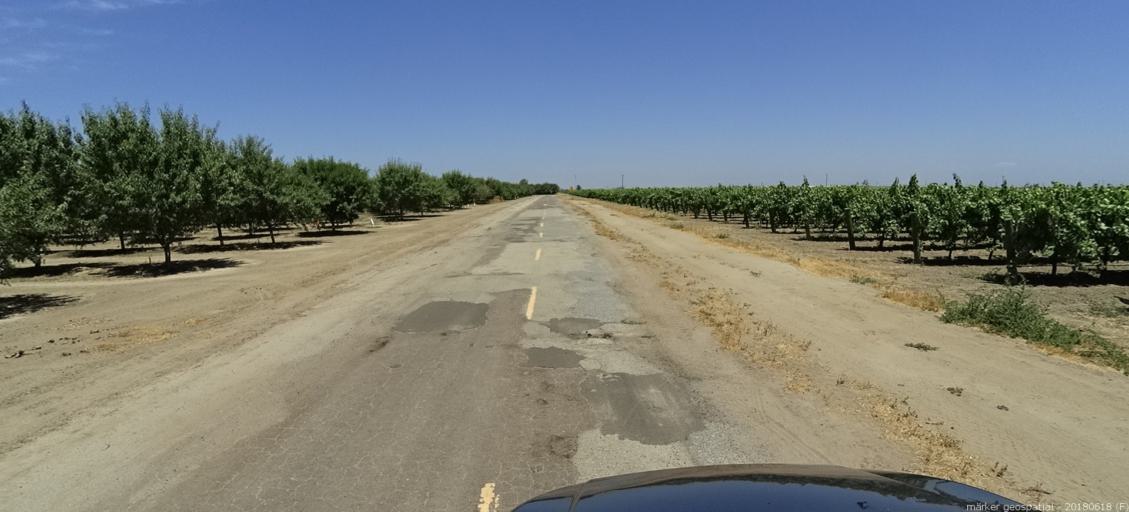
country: US
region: California
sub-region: Madera County
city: Parkwood
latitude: 36.9065
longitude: -120.1196
